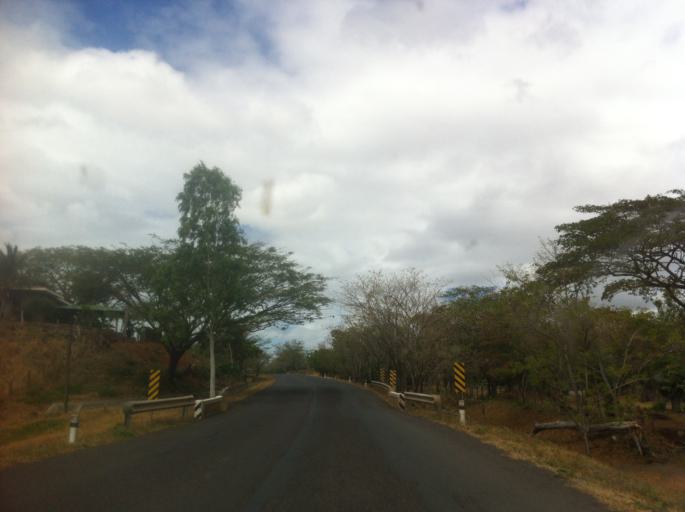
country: NI
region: Chontales
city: Juigalpa
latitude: 12.0823
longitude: -85.3249
